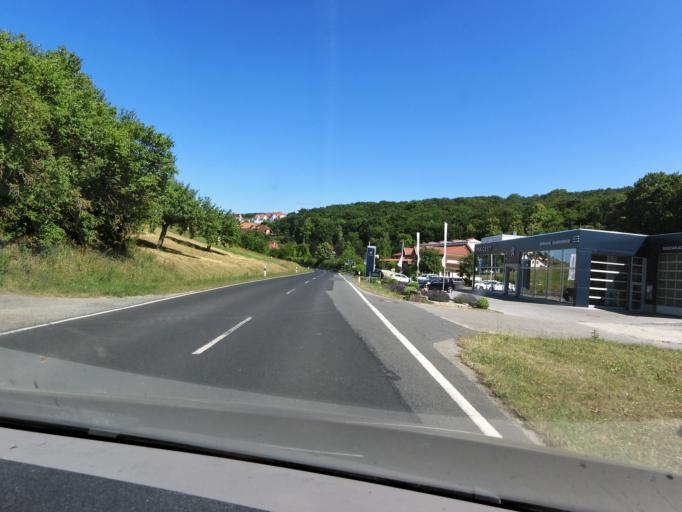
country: DE
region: Bavaria
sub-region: Regierungsbezirk Unterfranken
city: Theilheim
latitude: 49.7534
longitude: 10.0154
